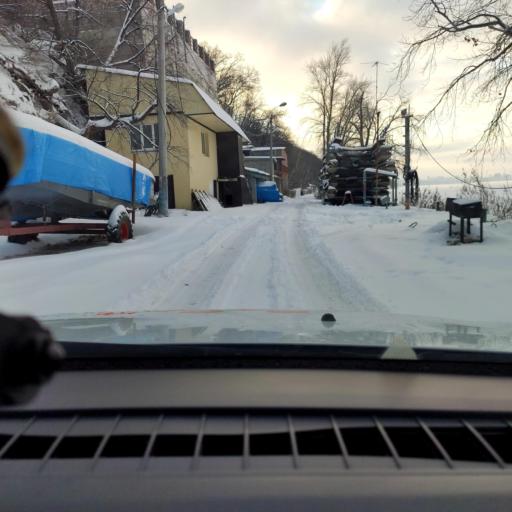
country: RU
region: Samara
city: Samara
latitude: 53.2914
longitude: 50.1921
